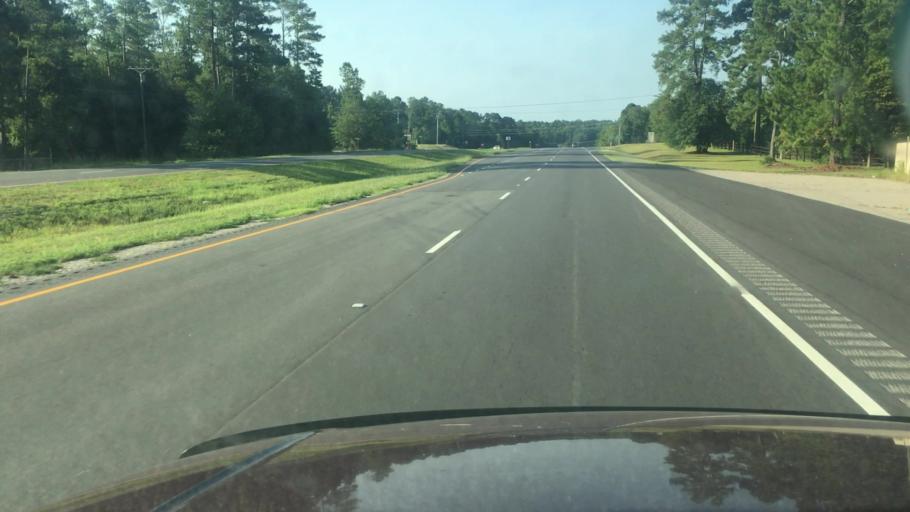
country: US
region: North Carolina
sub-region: Robeson County
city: Saint Pauls
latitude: 34.8661
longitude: -78.8503
